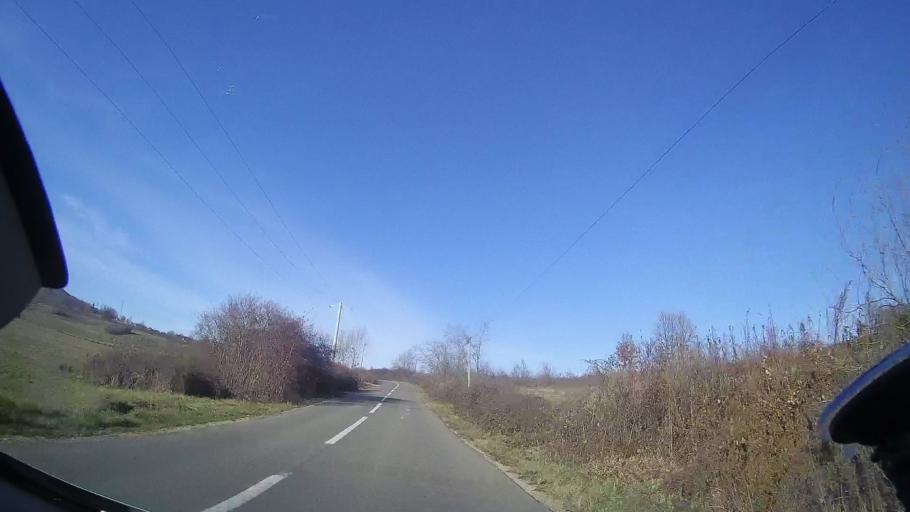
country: RO
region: Bihor
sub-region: Comuna Vadu Crisului
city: Vadu Crisului
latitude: 46.9702
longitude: 22.5477
